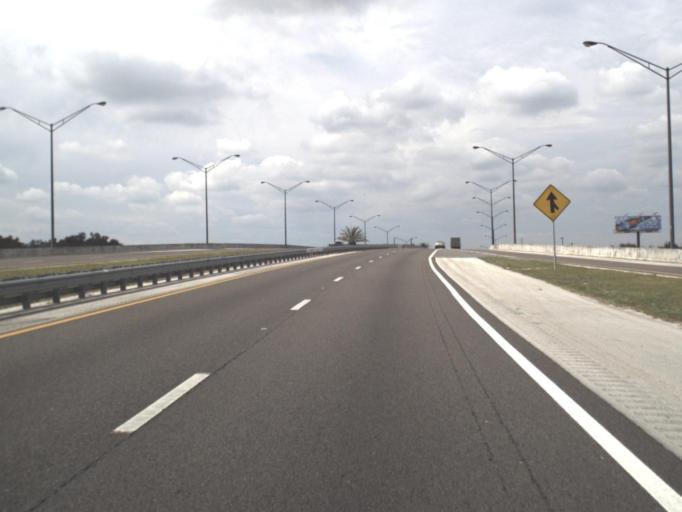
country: US
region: Florida
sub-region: Polk County
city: Medulla
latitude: 27.9965
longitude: -81.9798
